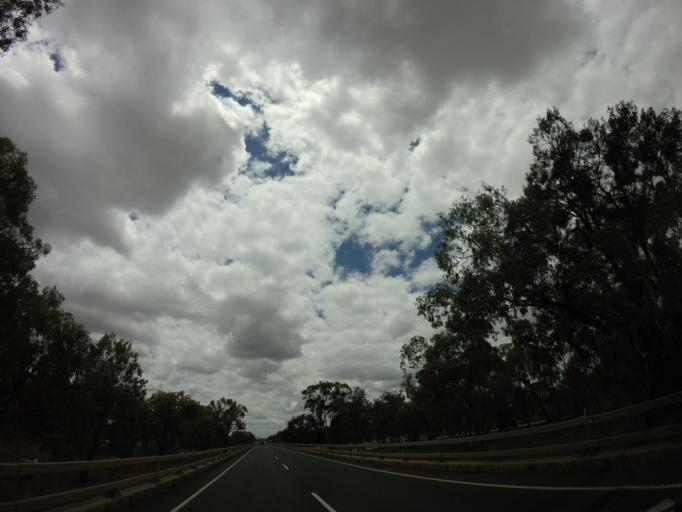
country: AU
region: Queensland
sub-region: Goondiwindi
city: Goondiwindi
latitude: -28.4001
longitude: 150.3094
